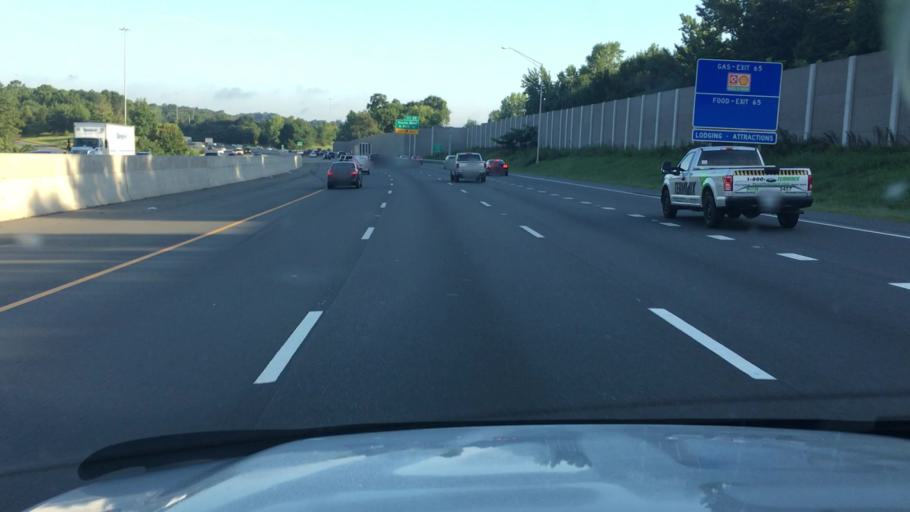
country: US
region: North Carolina
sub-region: Mecklenburg County
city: Pineville
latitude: 35.0967
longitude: -80.8763
